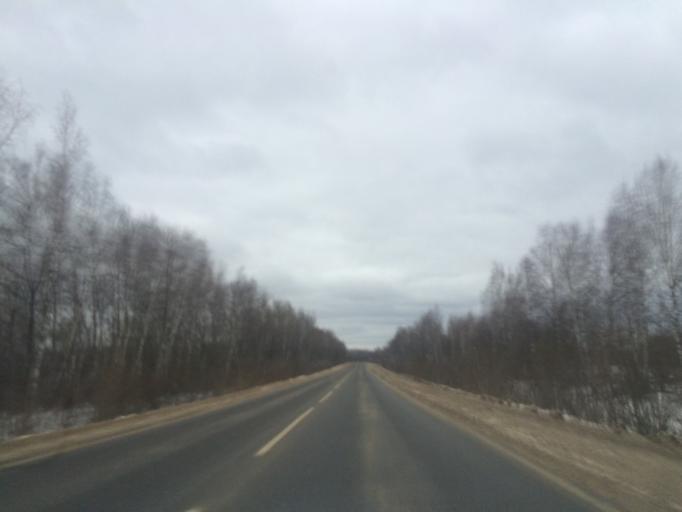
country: RU
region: Tula
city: Odoyev
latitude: 54.0053
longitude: 36.7670
